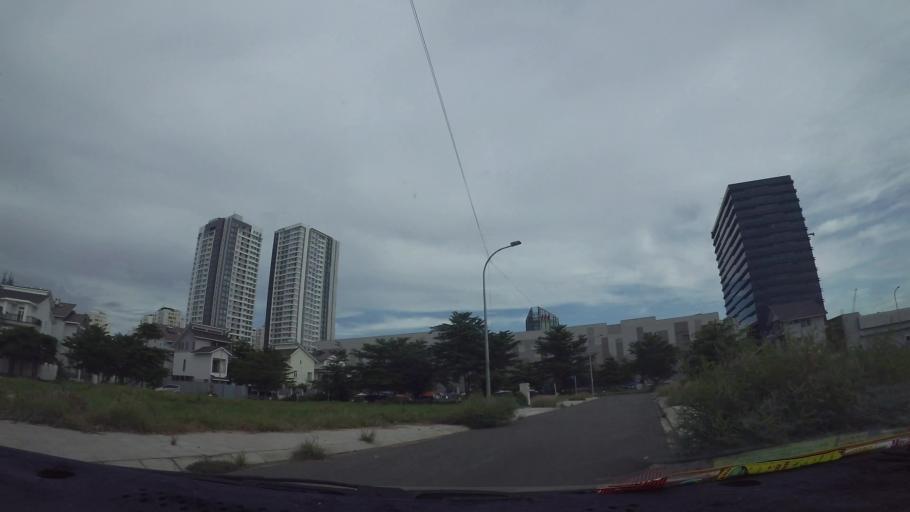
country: VN
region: Ho Chi Minh City
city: Quan Sau
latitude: 10.7426
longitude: 106.6505
